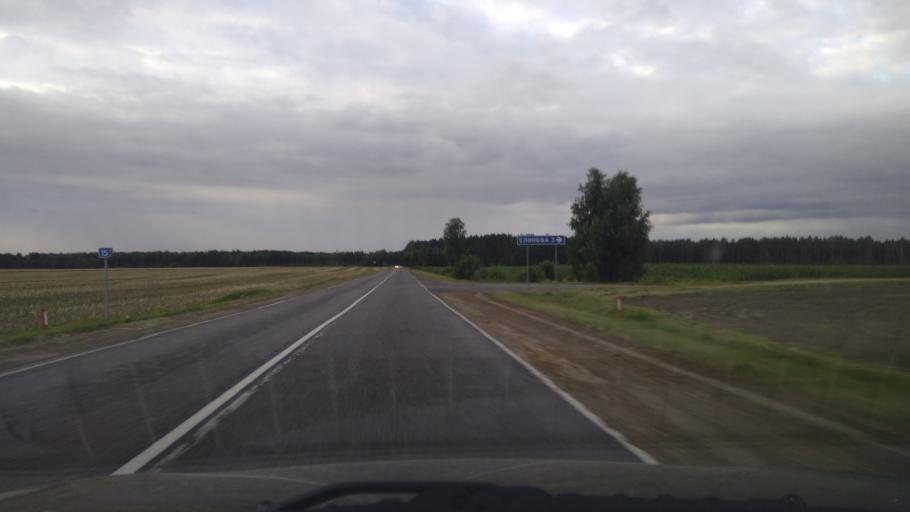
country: BY
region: Brest
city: Byaroza
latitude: 52.3982
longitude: 25.0055
